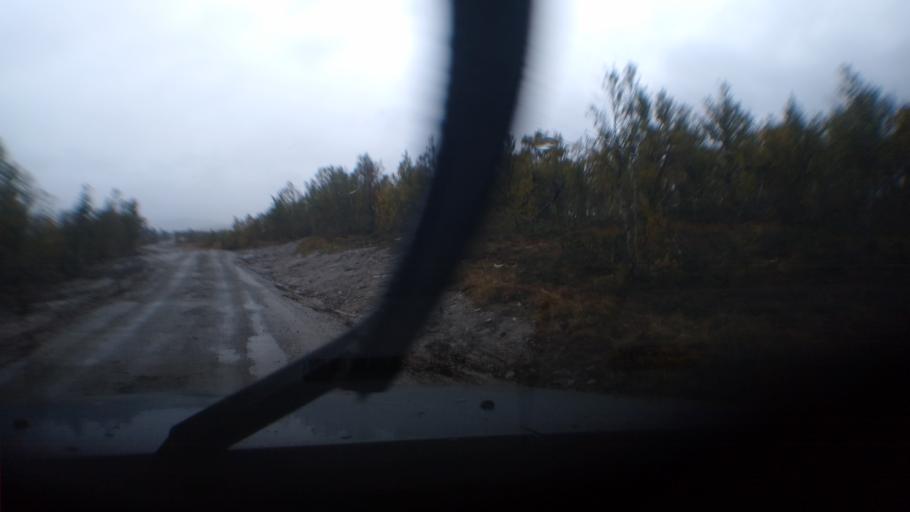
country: NO
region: Oppland
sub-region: Ringebu
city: Ringebu
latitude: 61.6566
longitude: 10.1037
